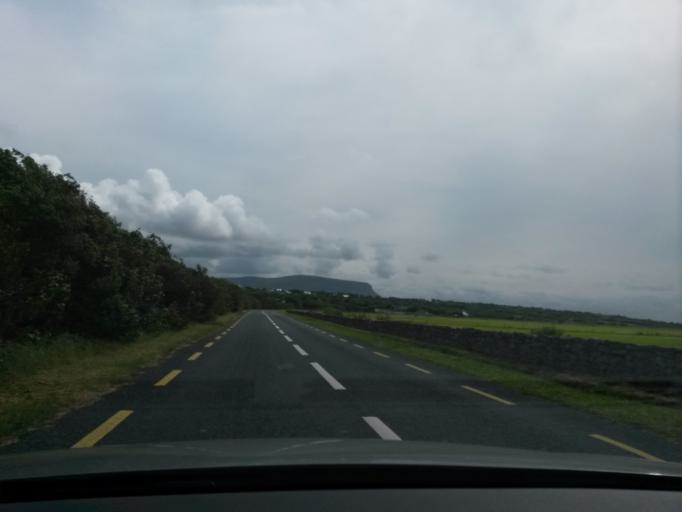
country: IE
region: Connaught
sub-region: Sligo
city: Sligo
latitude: 54.4386
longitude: -8.4553
